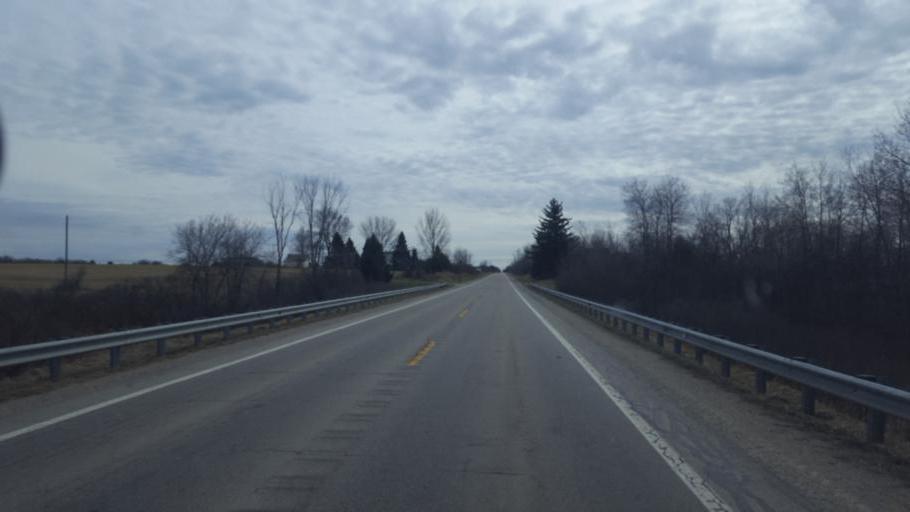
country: US
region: Michigan
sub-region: Isabella County
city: Lake Isabella
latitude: 43.7080
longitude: -85.1467
